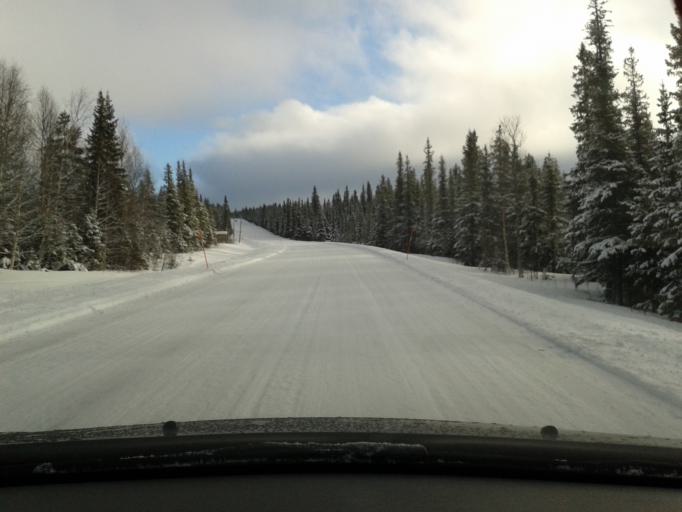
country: SE
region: Vaesterbotten
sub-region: Vilhelmina Kommun
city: Sjoberg
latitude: 65.2513
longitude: 15.6194
